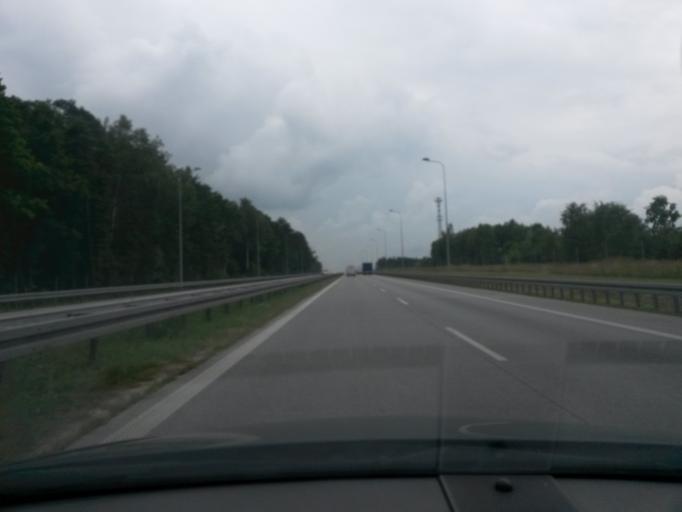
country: PL
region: Lodz Voivodeship
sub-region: Powiat rawski
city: Rawa Mazowiecka
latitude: 51.8238
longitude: 20.3219
